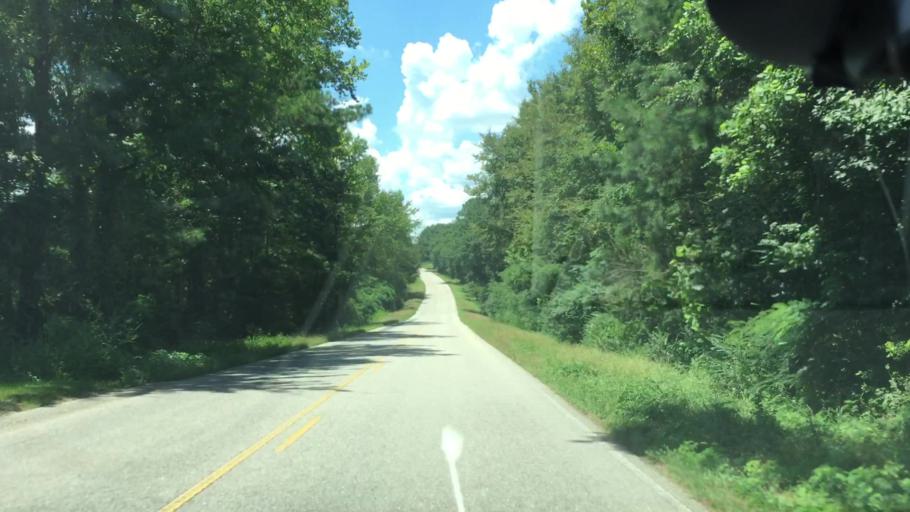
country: US
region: Alabama
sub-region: Pike County
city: Troy
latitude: 31.7462
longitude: -85.9649
